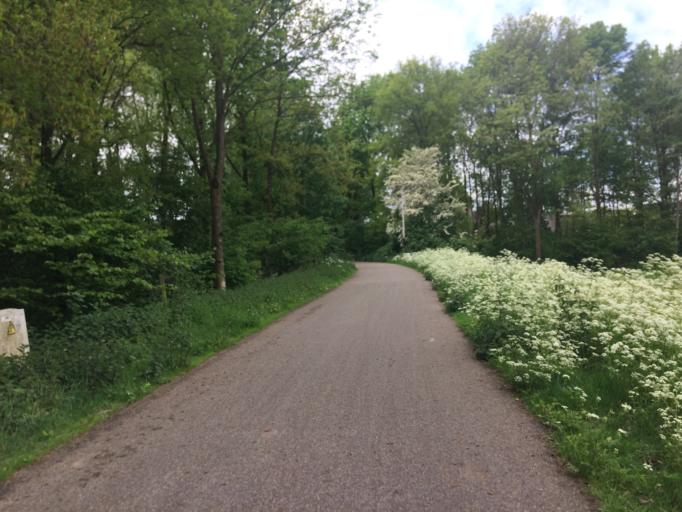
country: NL
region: Gelderland
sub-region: Gemeente Maasdriel
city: Hedel
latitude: 51.6962
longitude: 5.2299
